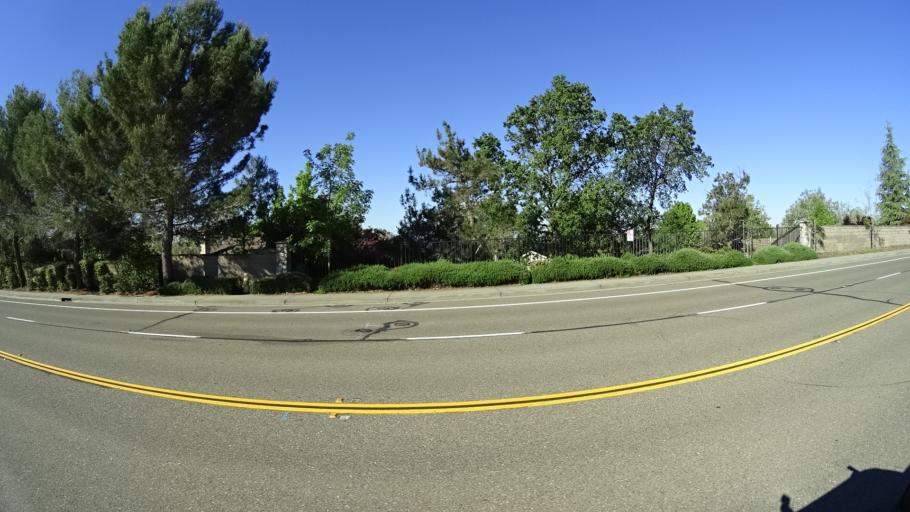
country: US
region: California
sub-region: Placer County
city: Loomis
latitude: 38.8368
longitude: -121.2305
